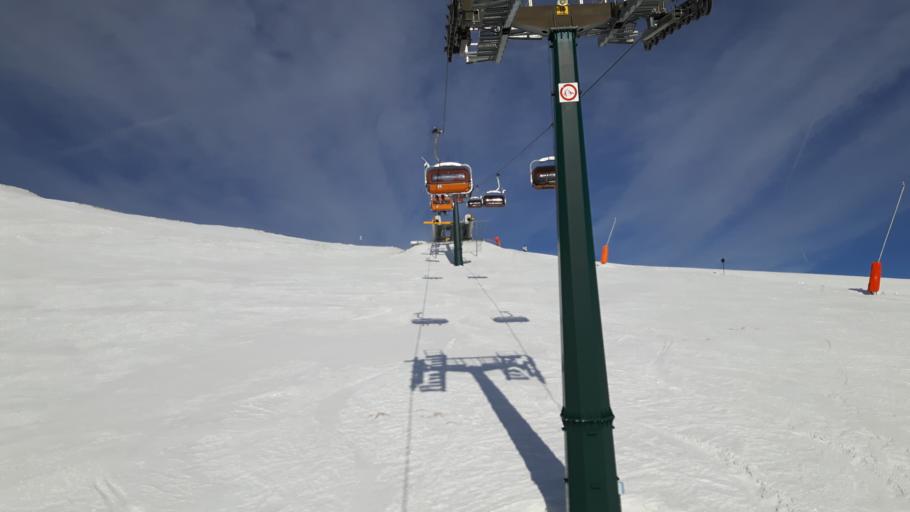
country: IT
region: Trentino-Alto Adige
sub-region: Provincia di Trento
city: Moena
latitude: 46.3426
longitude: 11.6950
